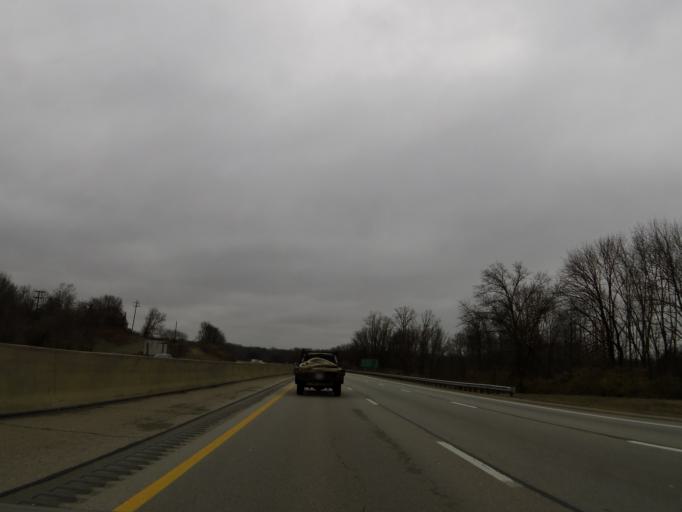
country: US
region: Kentucky
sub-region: Boone County
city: Walton
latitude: 38.8500
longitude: -84.6220
